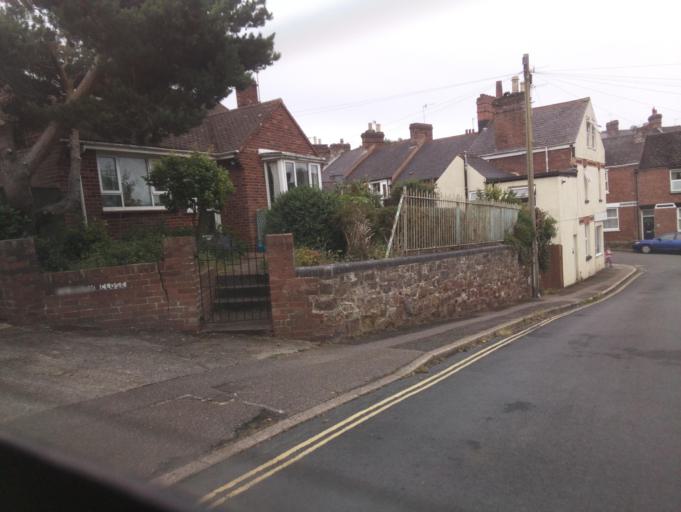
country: GB
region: England
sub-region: Devon
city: Exeter
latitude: 50.7192
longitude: -3.5243
